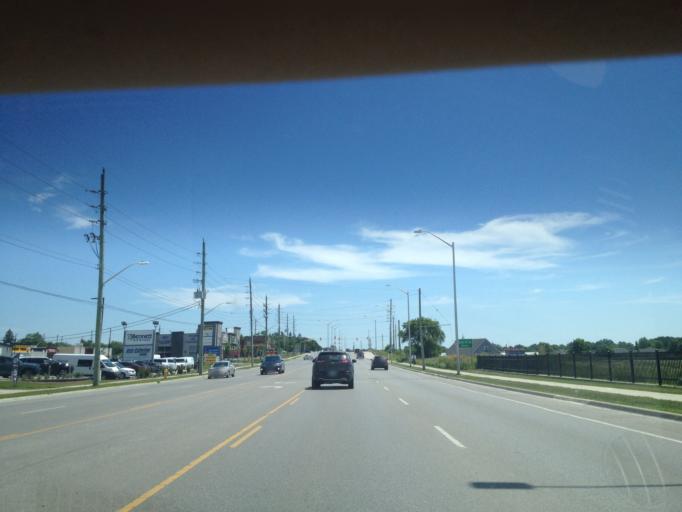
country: CA
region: Ontario
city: London
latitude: 42.9904
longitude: -81.3280
